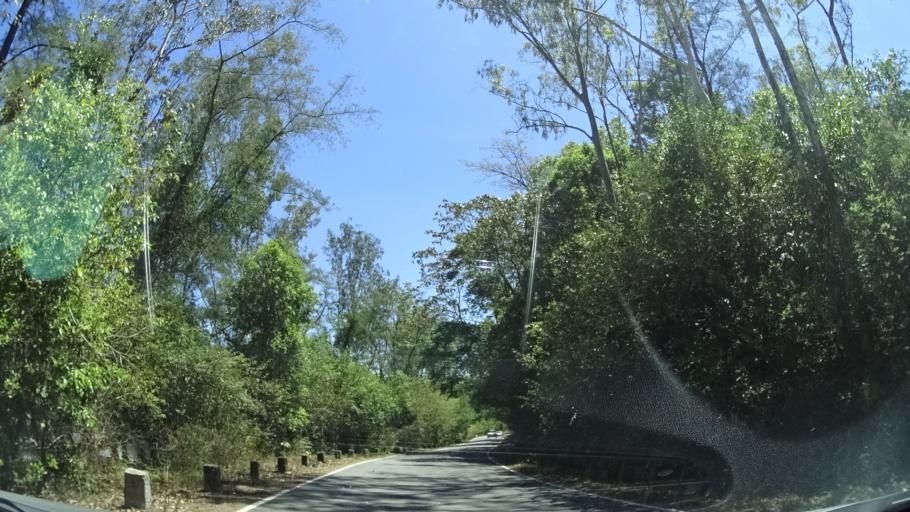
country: IN
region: Karnataka
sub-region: Chikmagalur
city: Sringeri
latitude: 13.2123
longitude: 75.2151
